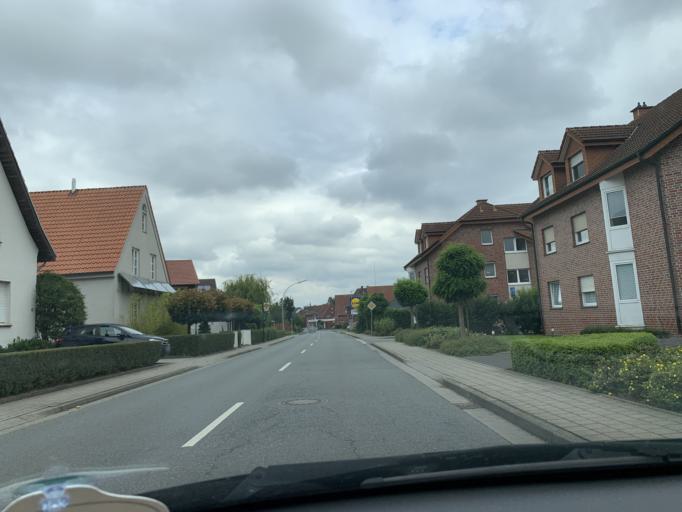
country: DE
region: North Rhine-Westphalia
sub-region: Regierungsbezirk Munster
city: Wadersloh
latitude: 51.7397
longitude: 8.2463
